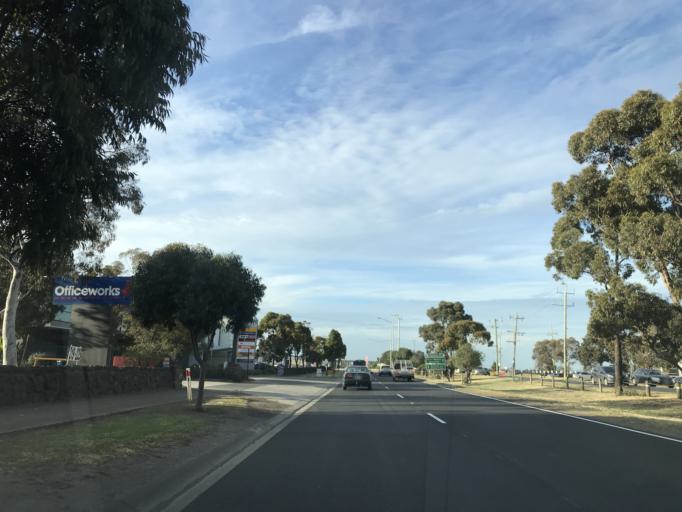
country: AU
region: Victoria
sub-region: Brimbank
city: Derrimut
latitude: -37.8154
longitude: 144.7870
